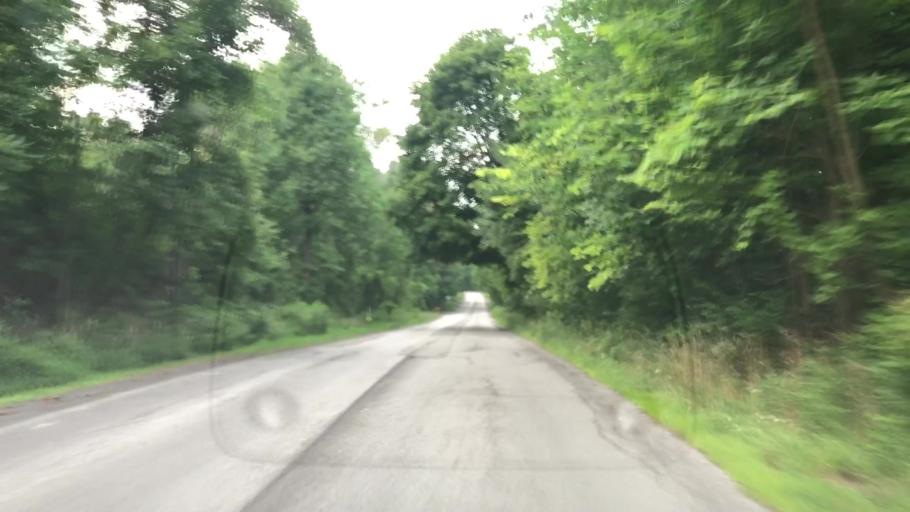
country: US
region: New York
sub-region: Erie County
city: East Aurora
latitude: 42.7844
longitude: -78.6046
